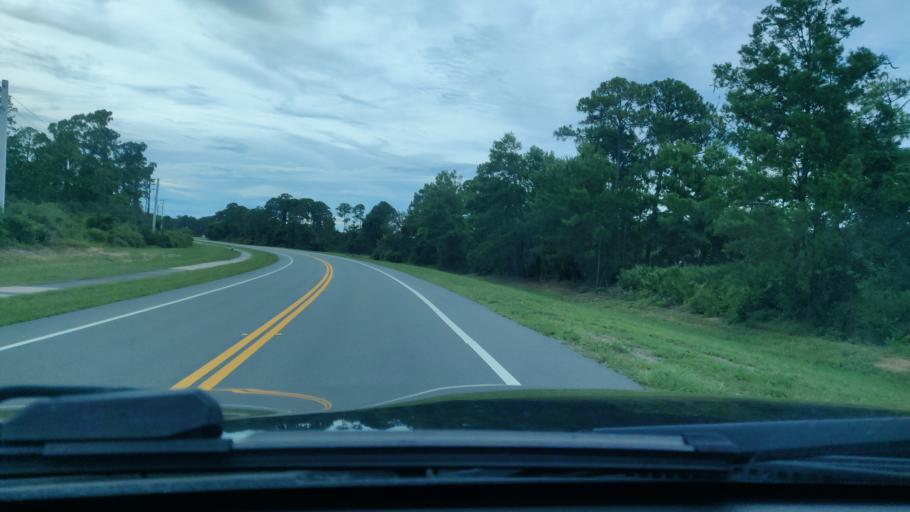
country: US
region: Florida
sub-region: Flagler County
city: Palm Coast
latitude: 29.5327
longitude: -81.1701
